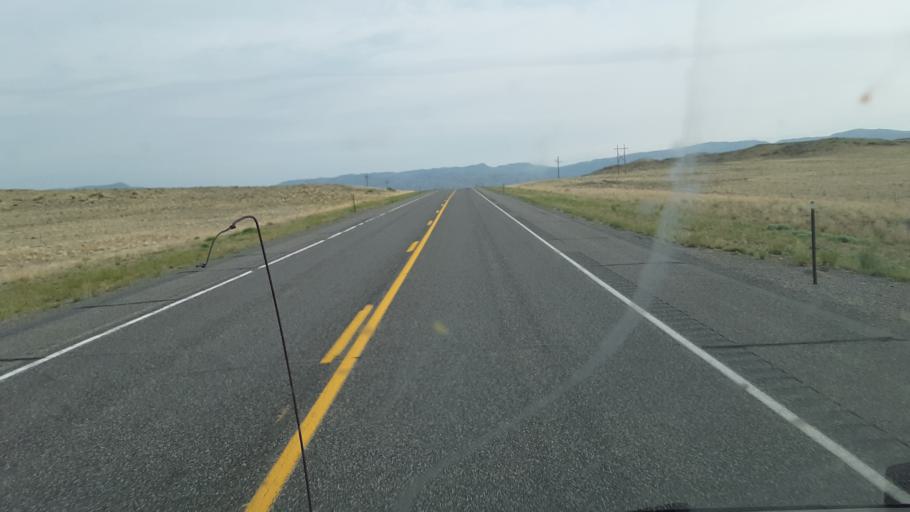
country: US
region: Wyoming
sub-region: Hot Springs County
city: Thermopolis
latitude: 43.3025
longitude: -108.1282
